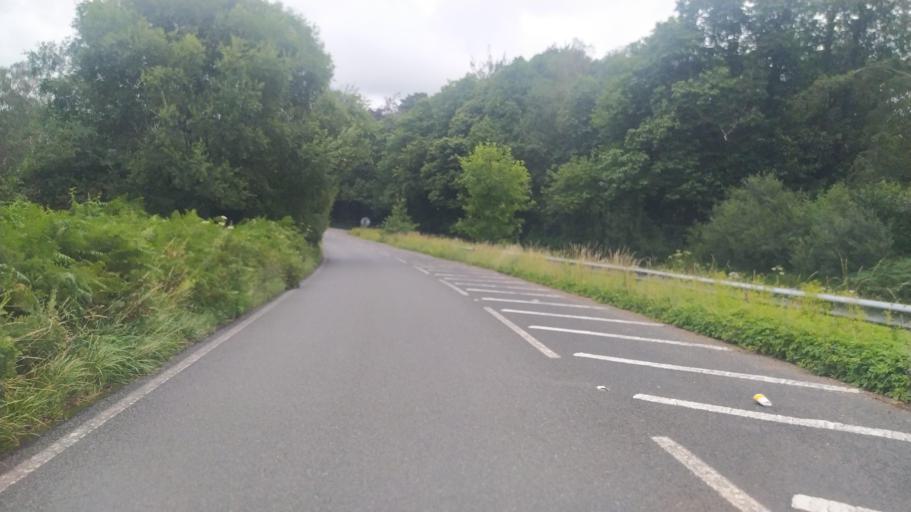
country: GB
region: England
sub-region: West Sussex
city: Milland
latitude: 51.0491
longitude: -0.8253
